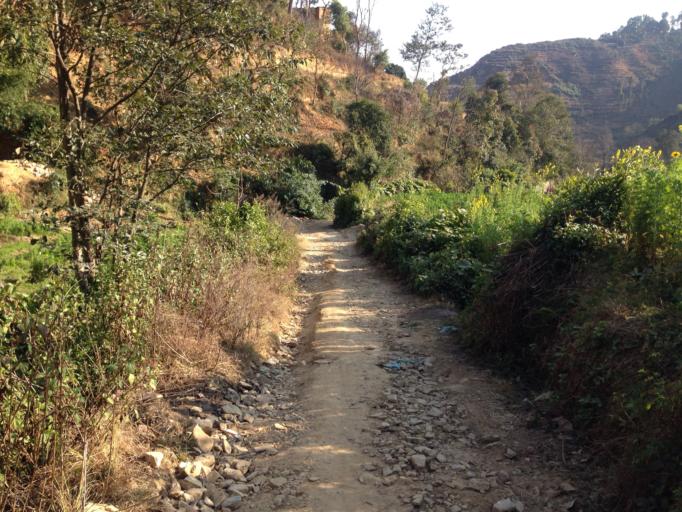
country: NP
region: Central Region
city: Kirtipur
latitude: 27.7308
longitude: 85.2658
